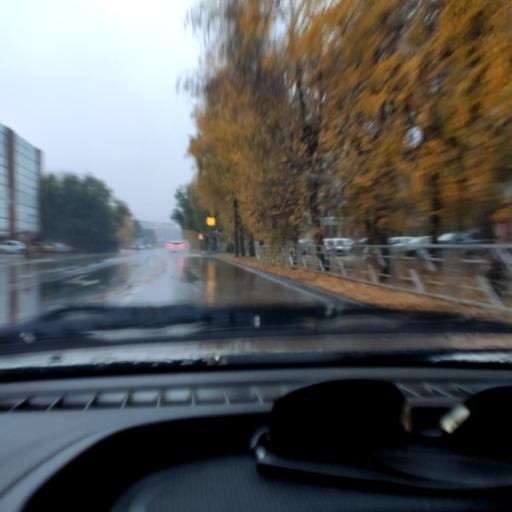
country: RU
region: Samara
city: Tol'yatti
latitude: 53.5322
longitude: 49.4303
